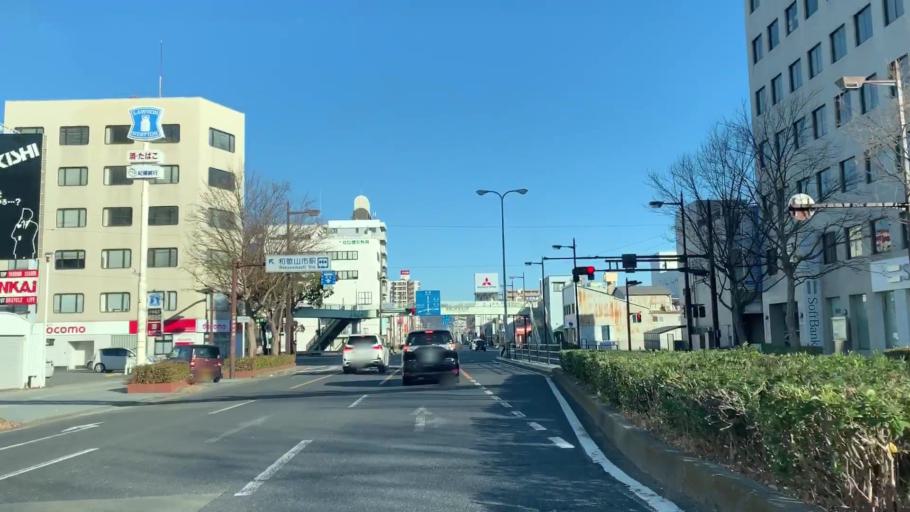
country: JP
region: Wakayama
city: Wakayama-shi
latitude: 34.2332
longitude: 135.1695
